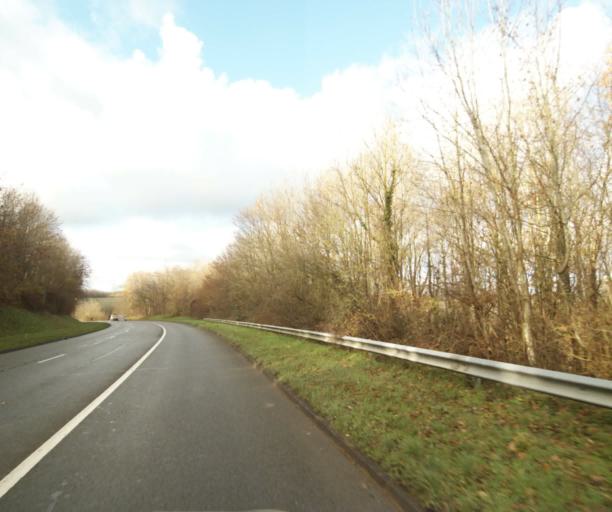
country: FR
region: Ile-de-France
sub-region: Departement des Yvelines
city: Meulan-en-Yvelines
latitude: 49.0151
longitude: 1.9219
